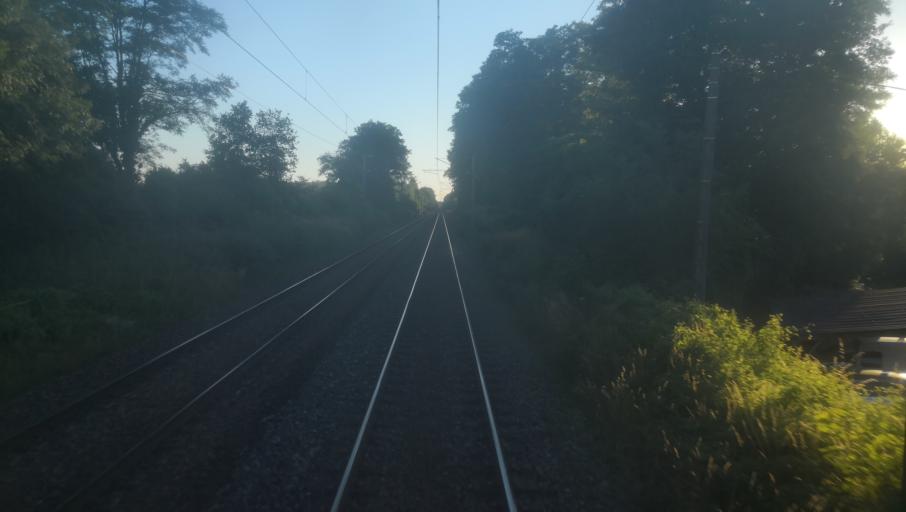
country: FR
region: Bourgogne
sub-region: Departement de la Nievre
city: Challuy
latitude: 46.9453
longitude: 3.1280
